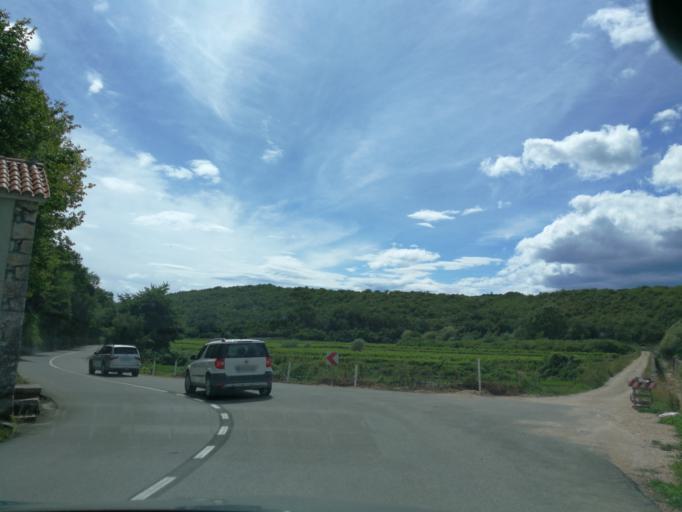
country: HR
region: Primorsko-Goranska
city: Punat
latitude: 45.0896
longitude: 14.6419
